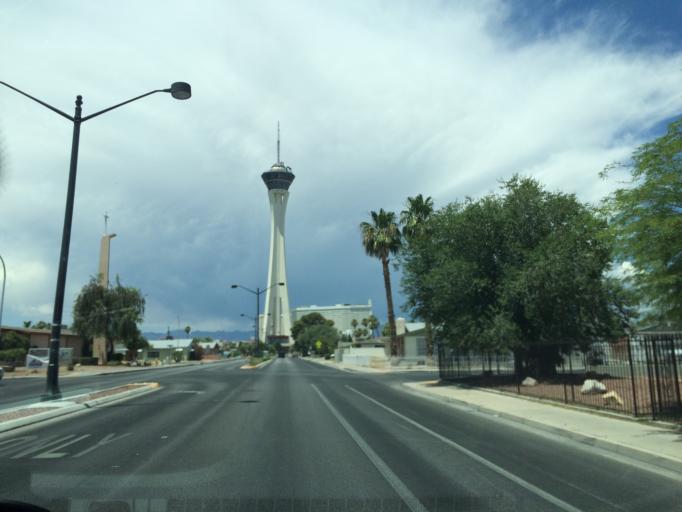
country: US
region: Nevada
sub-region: Clark County
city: Las Vegas
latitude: 36.1478
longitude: -115.1460
